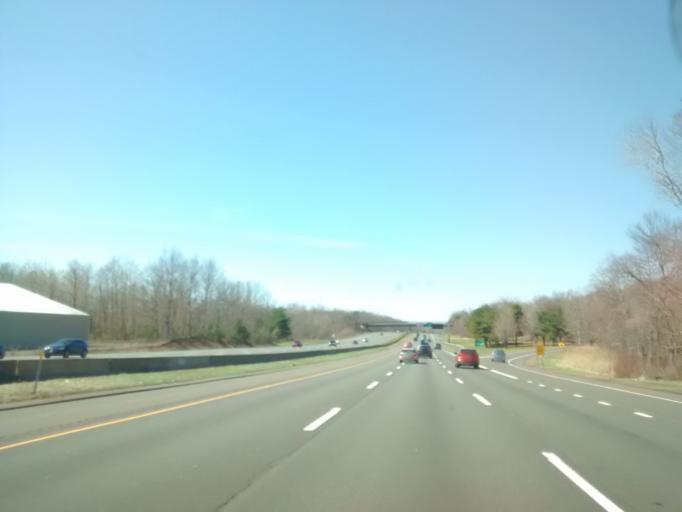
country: US
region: Connecticut
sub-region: Tolland County
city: Rockville
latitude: 41.8355
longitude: -72.4610
